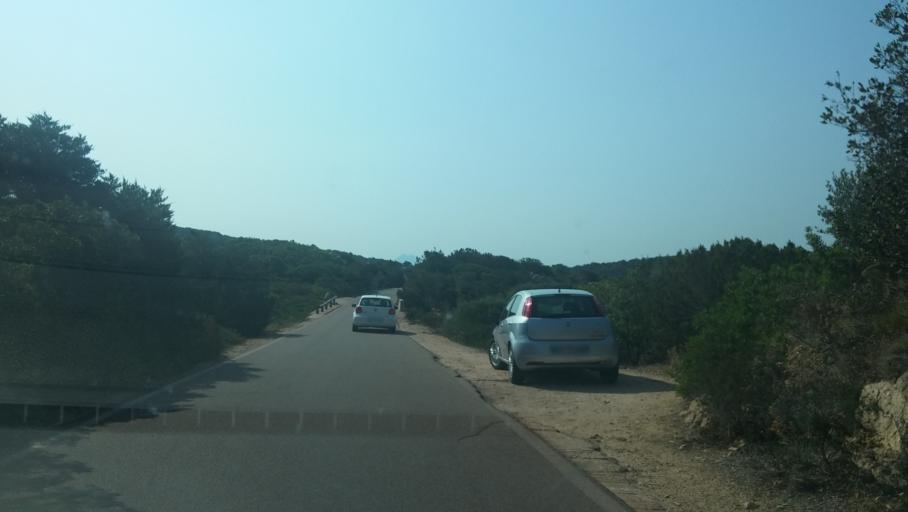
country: IT
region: Sardinia
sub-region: Provincia di Olbia-Tempio
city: La Maddalena
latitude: 41.1900
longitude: 9.4562
